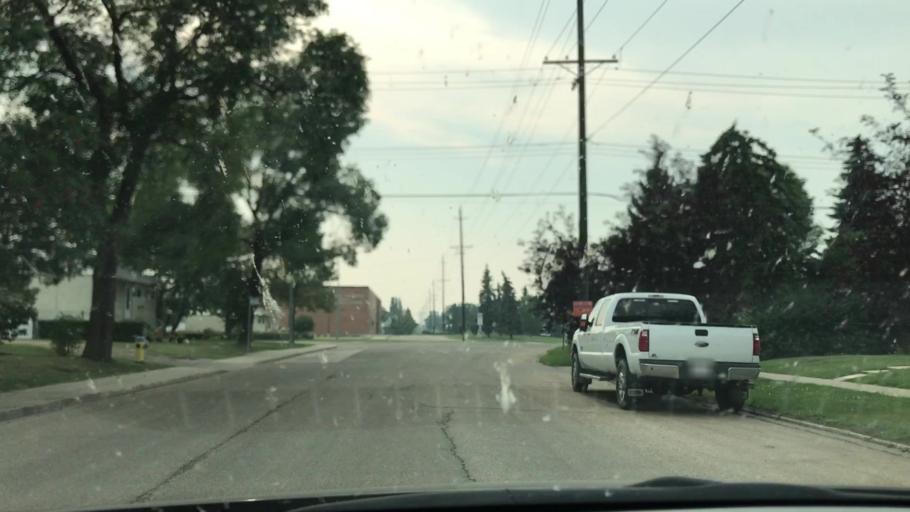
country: CA
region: Alberta
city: St. Albert
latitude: 53.5921
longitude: -113.5523
